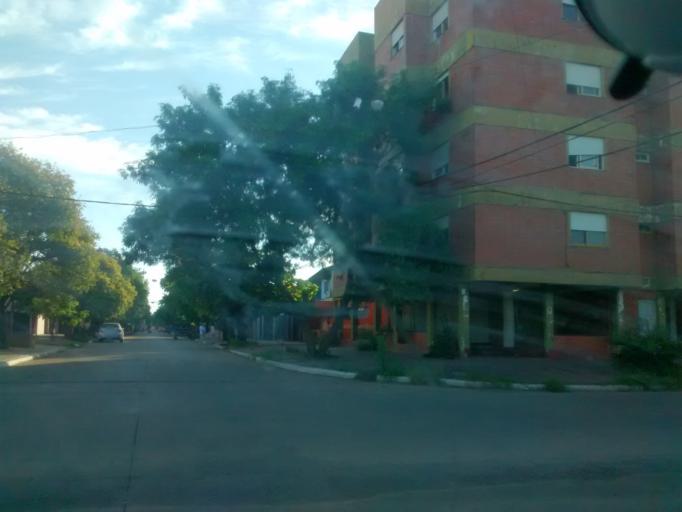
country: AR
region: Chaco
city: Resistencia
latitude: -27.4638
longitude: -58.9777
